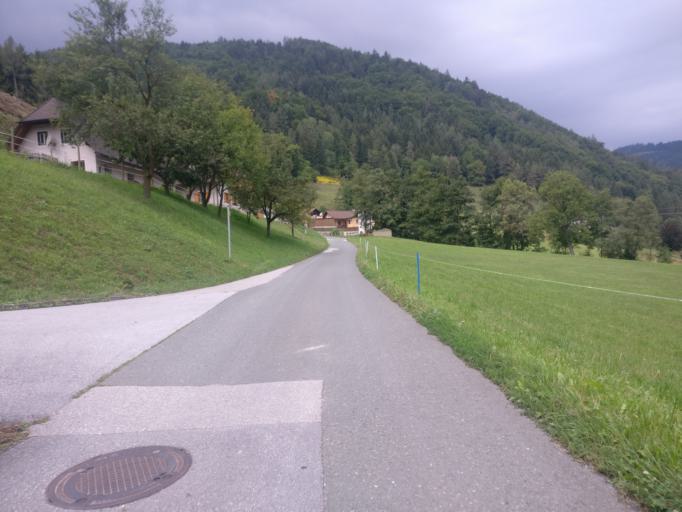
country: AT
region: Styria
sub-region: Politischer Bezirk Graz-Umgebung
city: Frohnleiten
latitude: 47.2388
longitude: 15.3109
